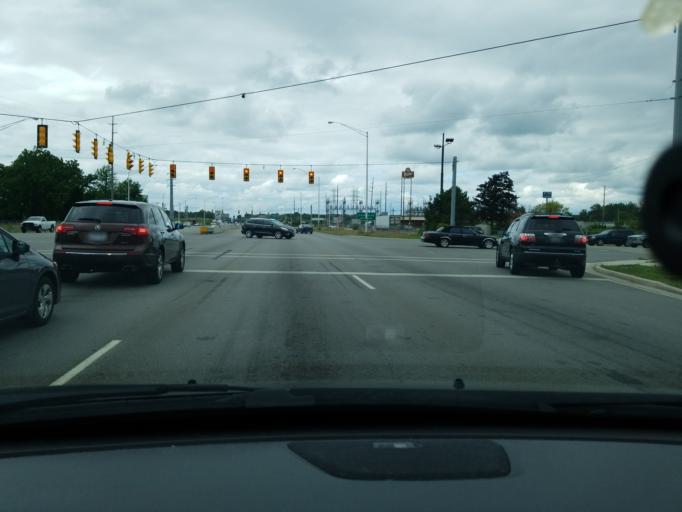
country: US
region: Ohio
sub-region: Lorain County
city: Sheffield
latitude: 41.3979
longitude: -82.1163
